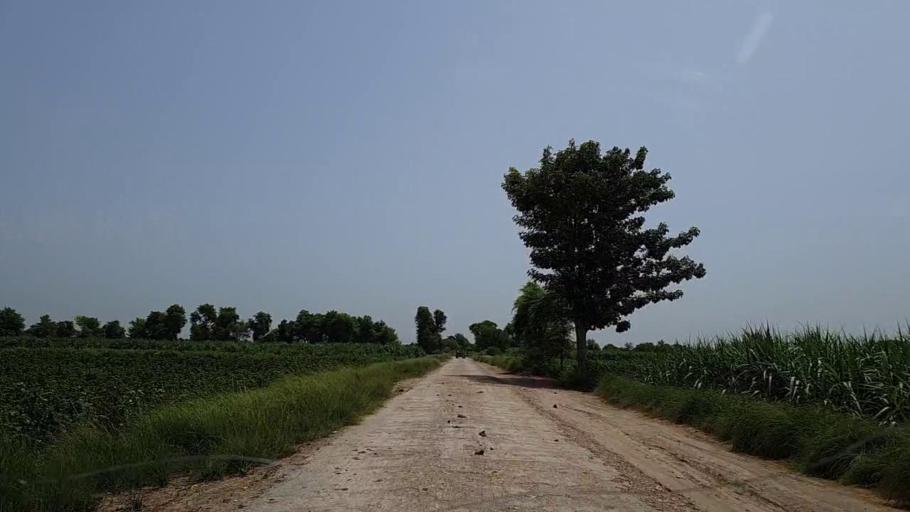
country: PK
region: Sindh
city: Naushahro Firoz
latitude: 26.8418
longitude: 67.9717
